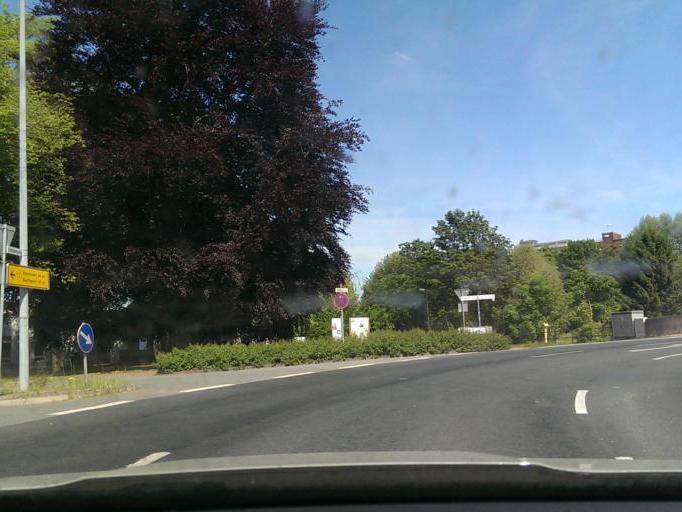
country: DE
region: Lower Saxony
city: Alfeld
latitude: 51.9815
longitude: 9.8208
